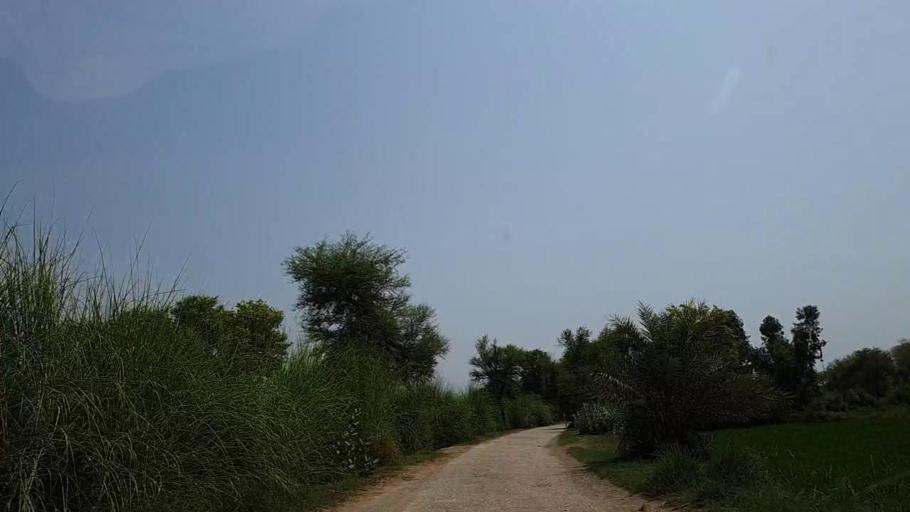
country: PK
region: Sindh
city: Adilpur
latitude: 27.9087
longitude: 69.3645
